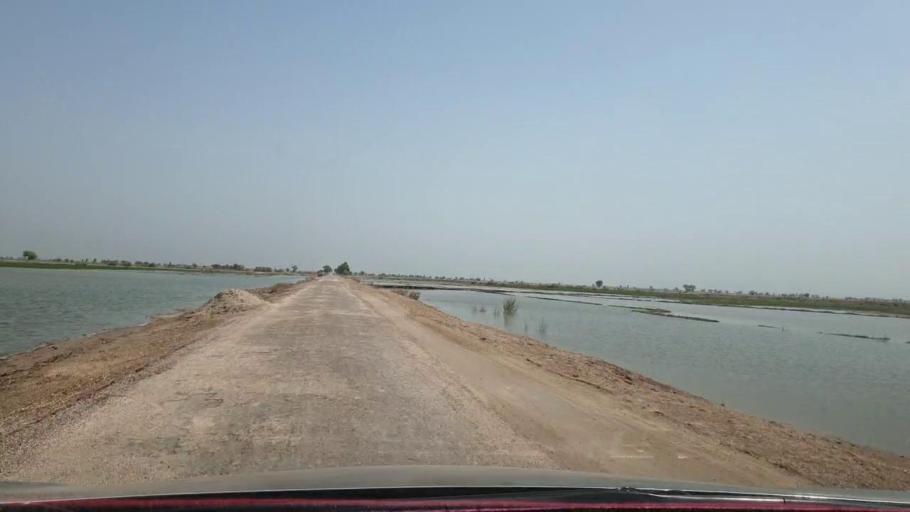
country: PK
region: Sindh
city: Warah
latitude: 27.3855
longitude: 67.7817
